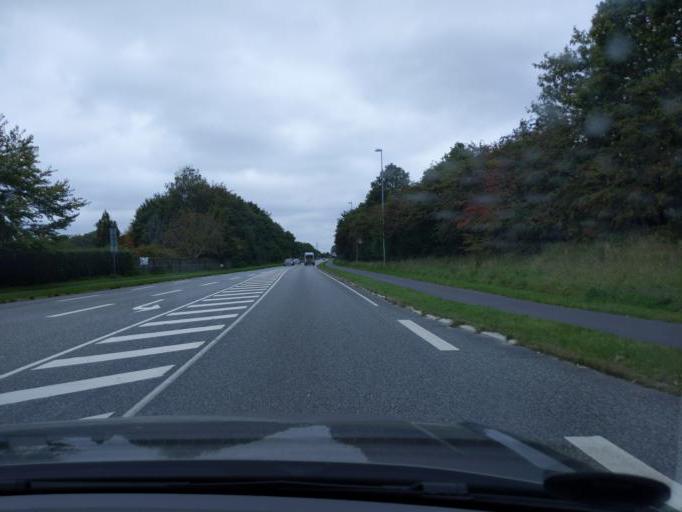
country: DK
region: Central Jutland
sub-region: Randers Kommune
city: Randers
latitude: 56.4838
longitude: 9.9935
